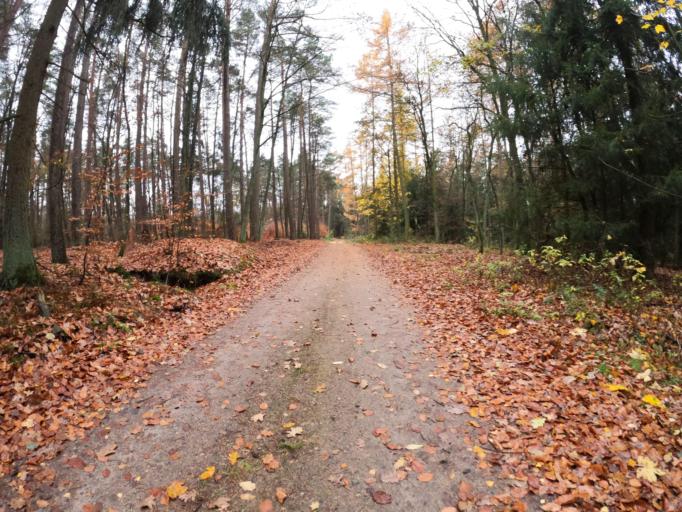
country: PL
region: West Pomeranian Voivodeship
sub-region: Powiat walecki
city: Tuczno
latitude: 53.2675
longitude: 16.2406
